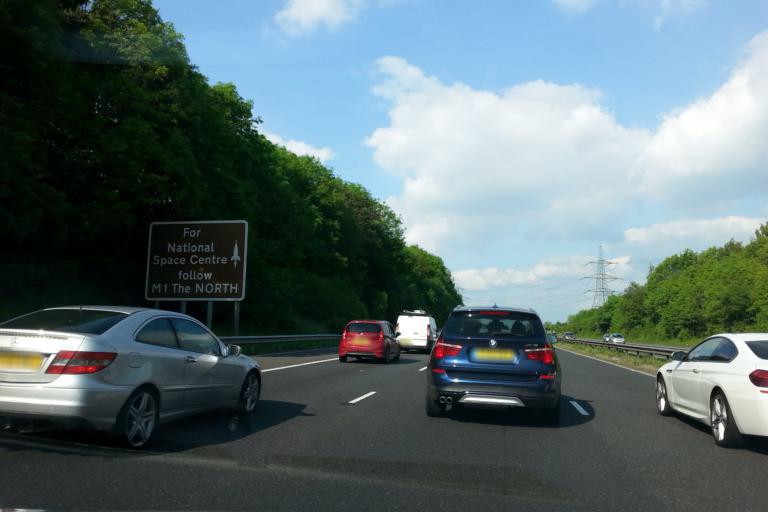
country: GB
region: England
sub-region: Leicestershire
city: Enderby
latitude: 52.5870
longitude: -1.2376
